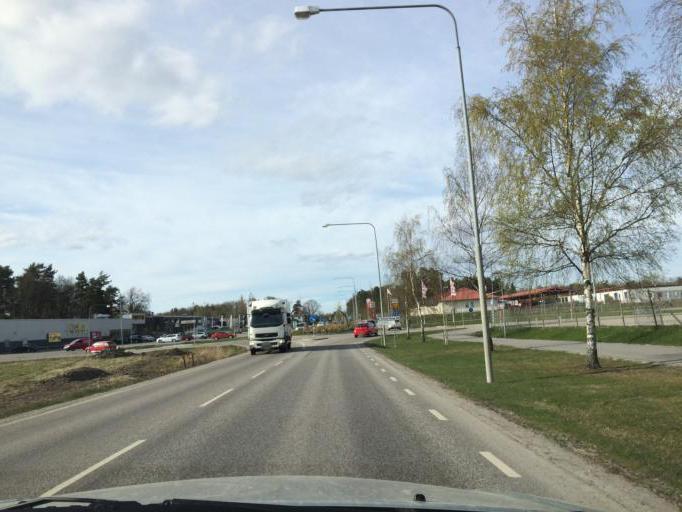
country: SE
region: Soedermanland
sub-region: Eskilstuna Kommun
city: Torshalla
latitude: 59.4095
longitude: 16.4775
